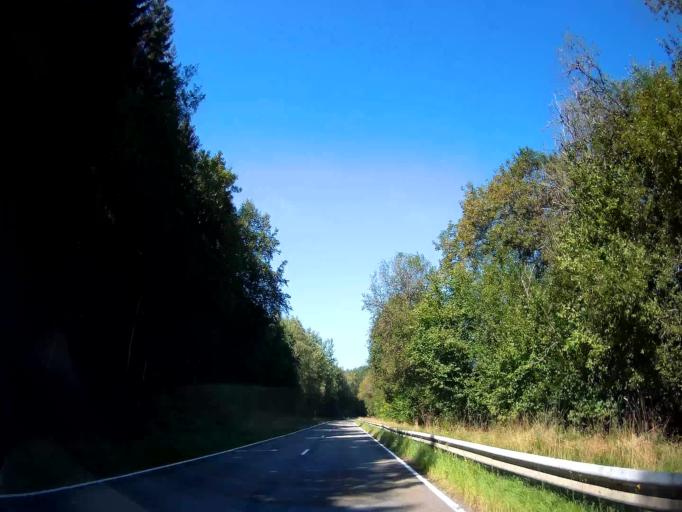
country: BE
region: Wallonia
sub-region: Province du Luxembourg
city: Bertogne
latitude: 50.1063
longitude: 5.6347
